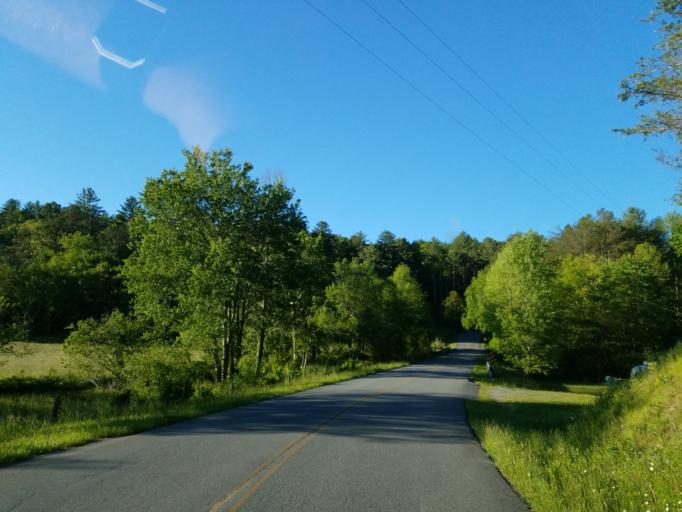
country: US
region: Georgia
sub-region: Fannin County
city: Blue Ridge
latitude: 34.7669
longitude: -84.2643
